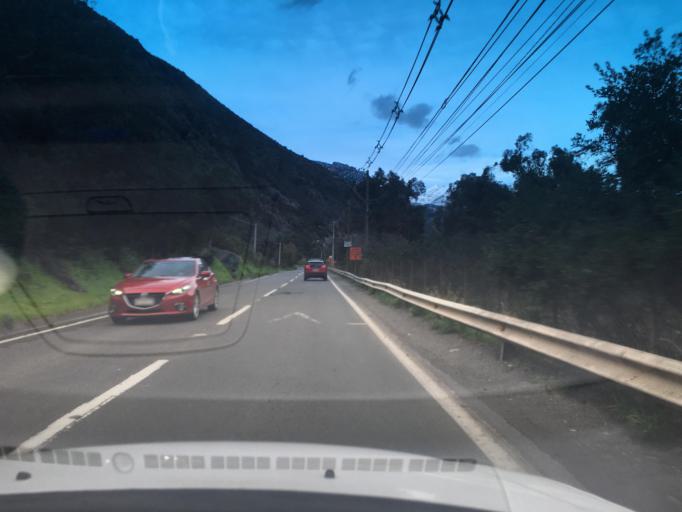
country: CL
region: Santiago Metropolitan
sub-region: Provincia de Cordillera
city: Puente Alto
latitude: -33.5776
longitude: -70.4304
